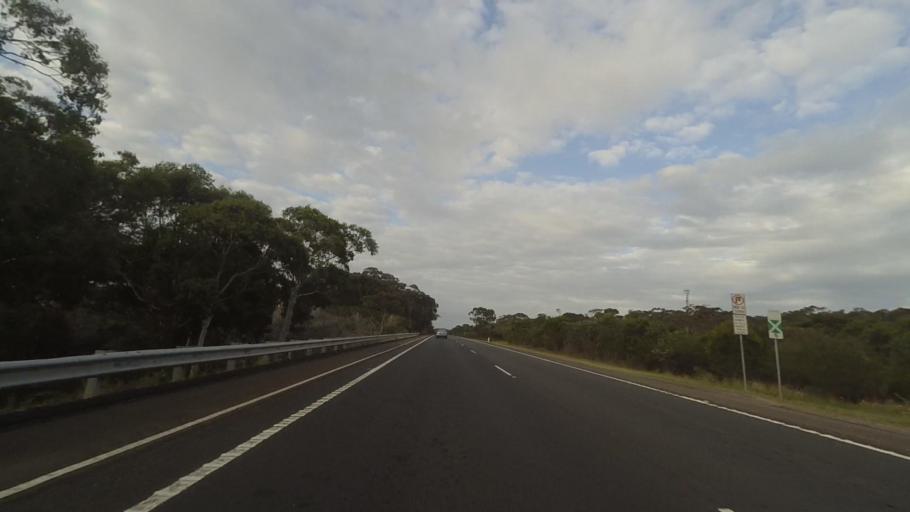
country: AU
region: New South Wales
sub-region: Wollongong
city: Bulli
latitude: -34.2602
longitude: 150.9295
